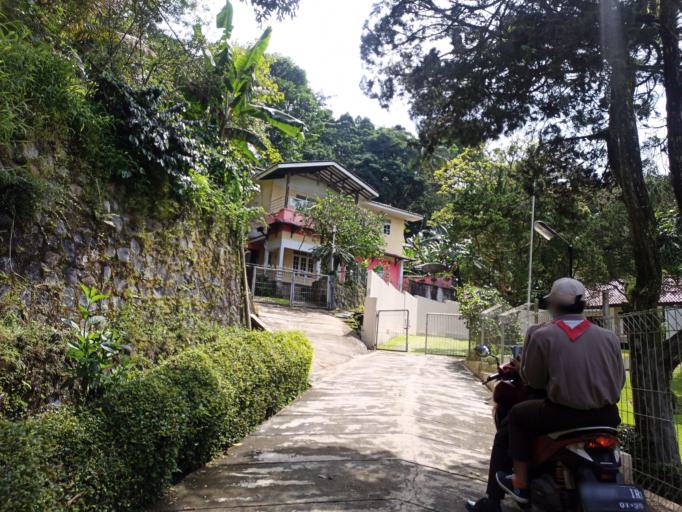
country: ID
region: West Java
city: Caringin
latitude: -6.6441
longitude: 106.9115
